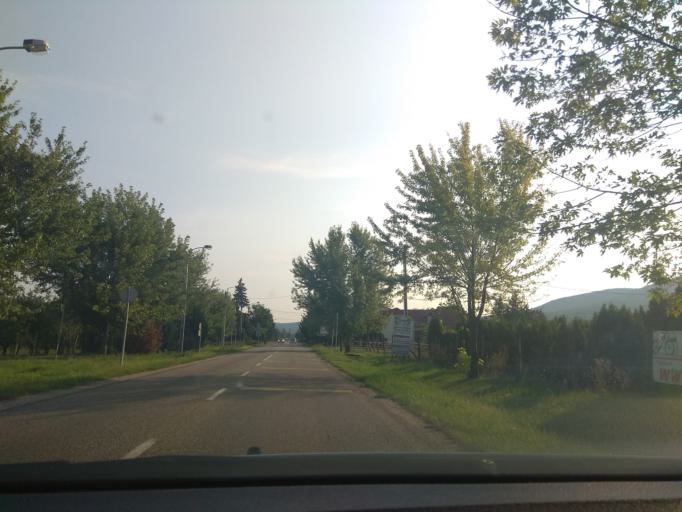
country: HU
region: Heves
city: Felsotarkany
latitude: 47.9608
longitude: 20.3996
